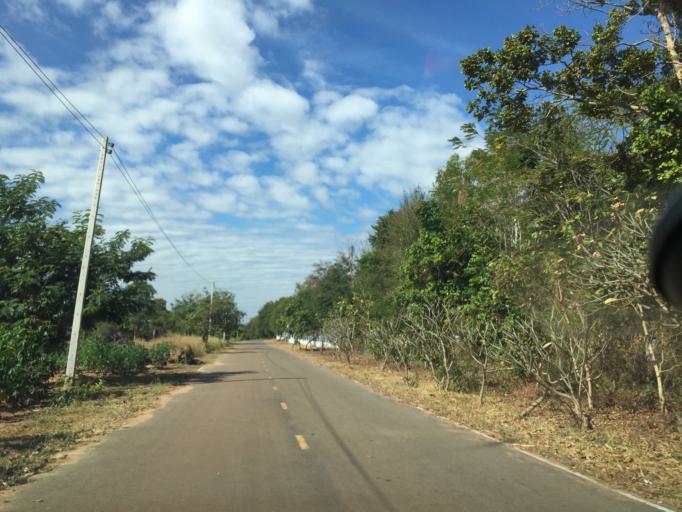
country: TH
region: Kalasin
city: Tha Khantho
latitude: 16.9717
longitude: 103.2704
